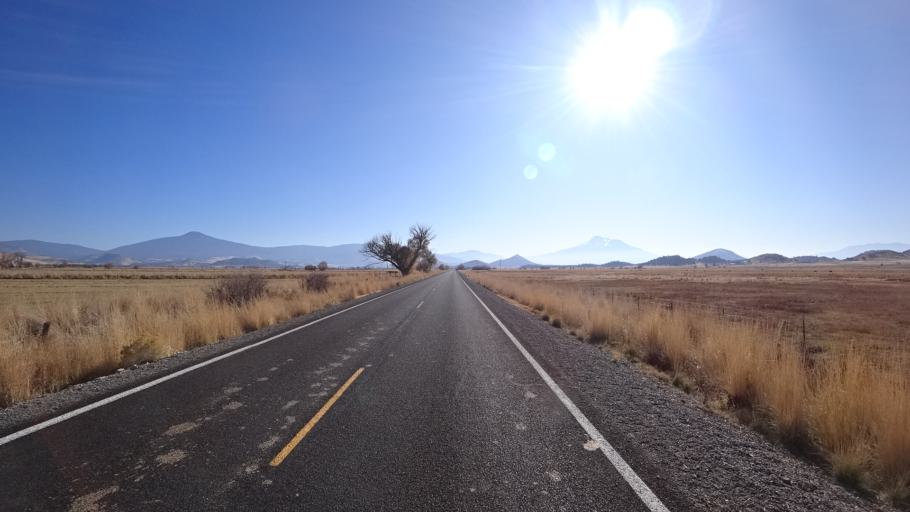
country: US
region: California
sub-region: Siskiyou County
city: Montague
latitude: 41.7146
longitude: -122.4425
